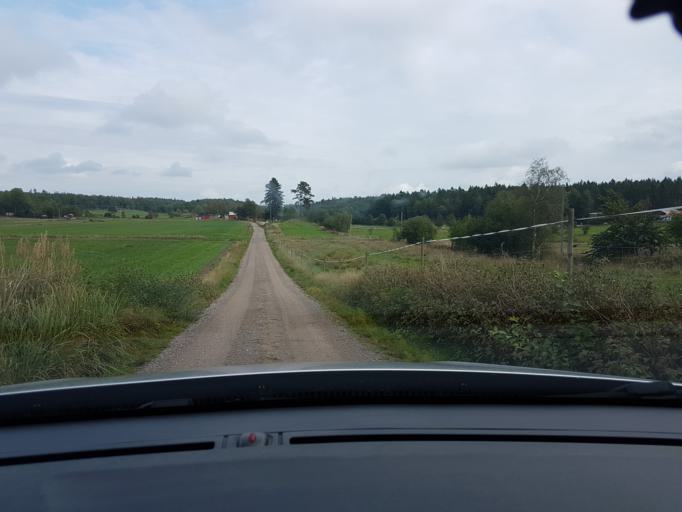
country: SE
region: Vaestra Goetaland
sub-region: Ale Kommun
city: Skepplanda
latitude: 57.8907
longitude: 12.1981
